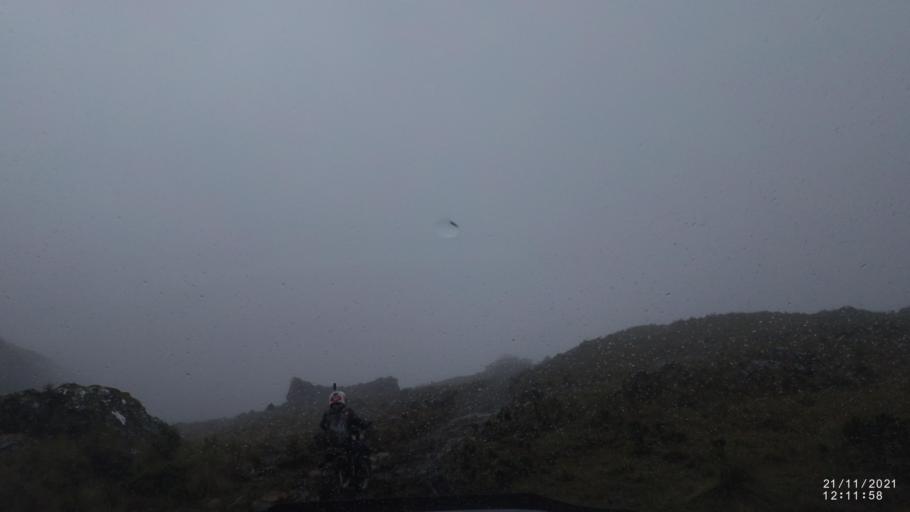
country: BO
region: Cochabamba
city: Cochabamba
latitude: -16.9434
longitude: -66.2561
